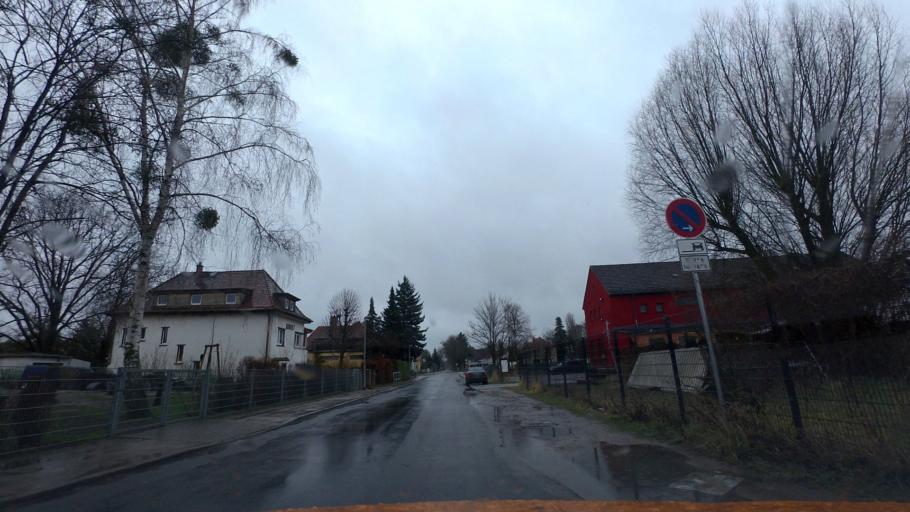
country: DE
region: Brandenburg
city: Brieselang
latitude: 52.5839
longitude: 13.0009
